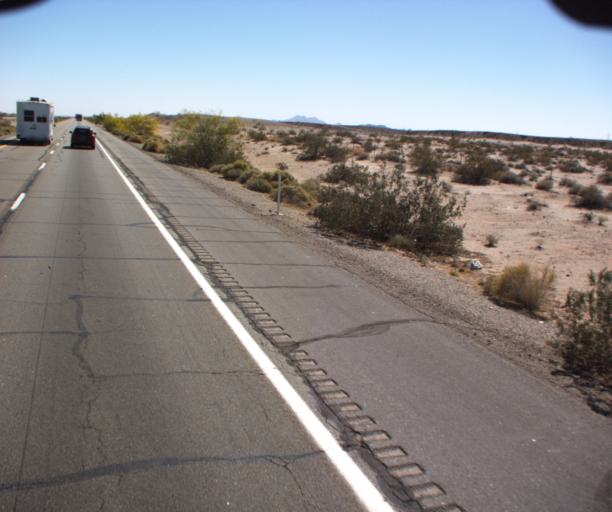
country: US
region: Arizona
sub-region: Yuma County
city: Wellton
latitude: 32.6563
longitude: -114.2407
